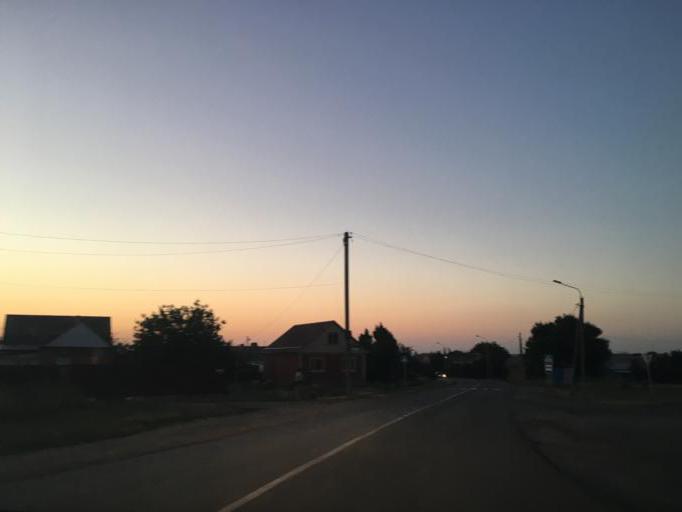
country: RU
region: Krasnodarskiy
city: Kushchevskaya
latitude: 46.5451
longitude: 39.6335
